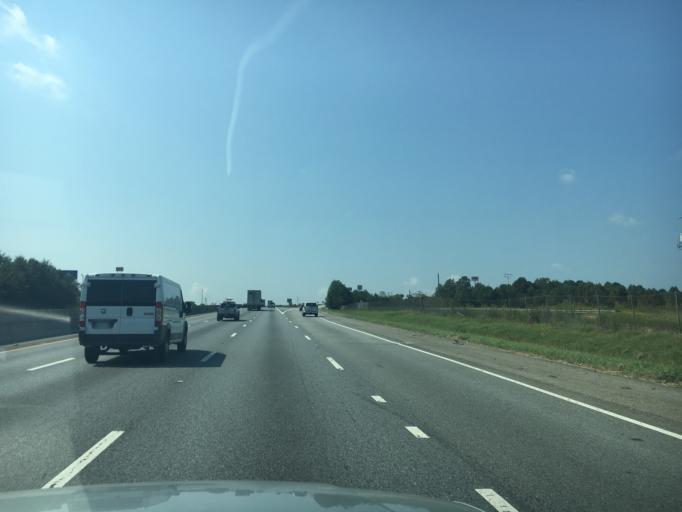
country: US
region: South Carolina
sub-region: Anderson County
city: Powdersville
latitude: 34.7785
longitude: -82.4593
